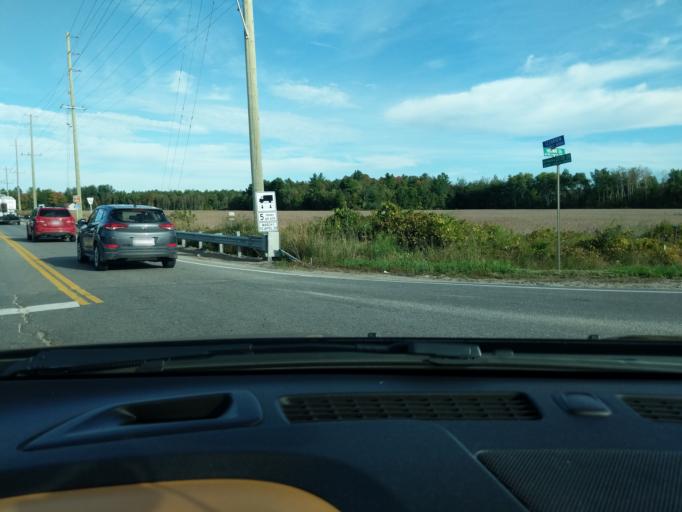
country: CA
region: Ontario
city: Wasaga Beach
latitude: 44.4347
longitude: -80.0996
